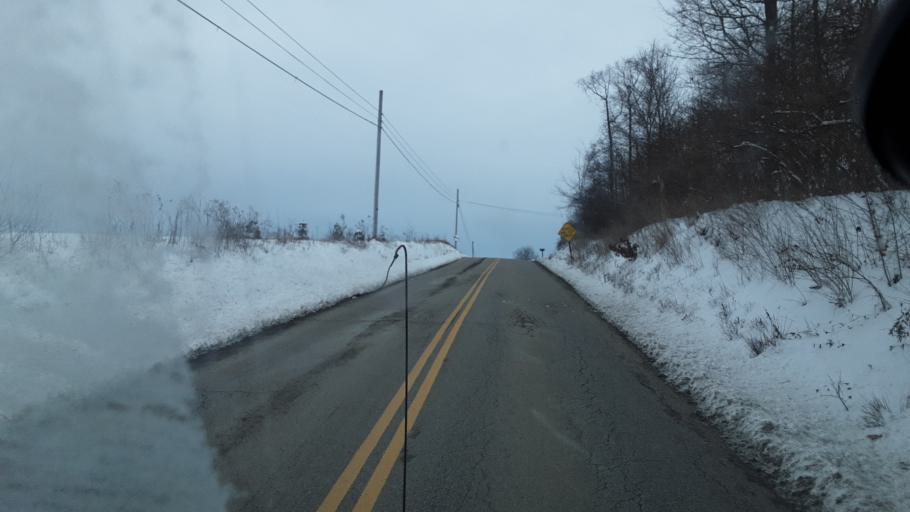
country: US
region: Ohio
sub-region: Perry County
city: Somerset
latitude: 39.9264
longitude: -82.2241
